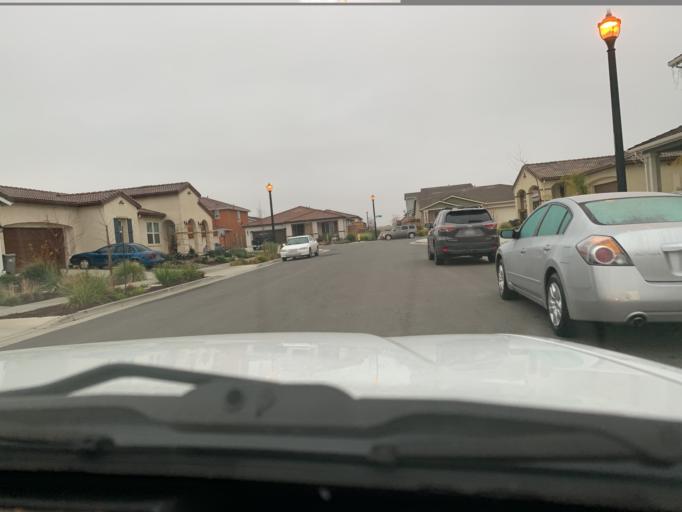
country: US
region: California
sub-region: Yolo County
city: Woodland
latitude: 38.6463
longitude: -121.7457
